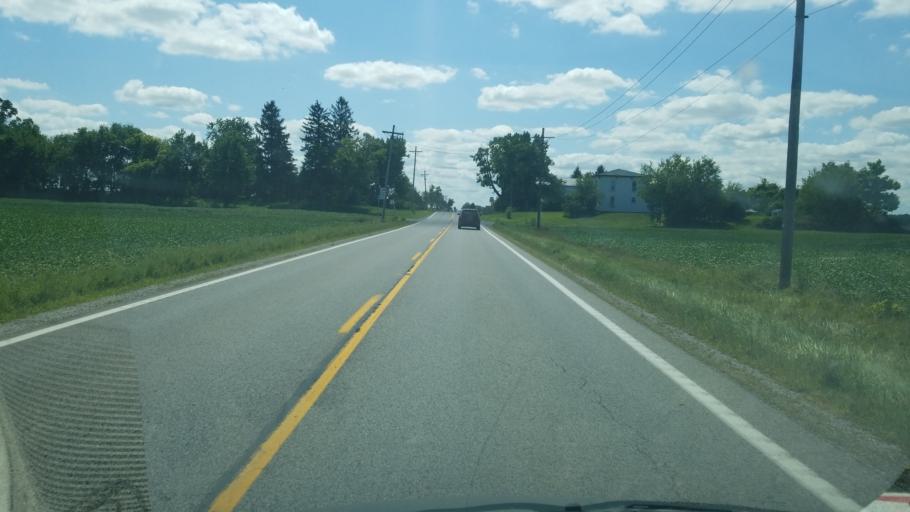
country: US
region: Ohio
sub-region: Fulton County
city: Delta
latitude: 41.6577
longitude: -84.0355
